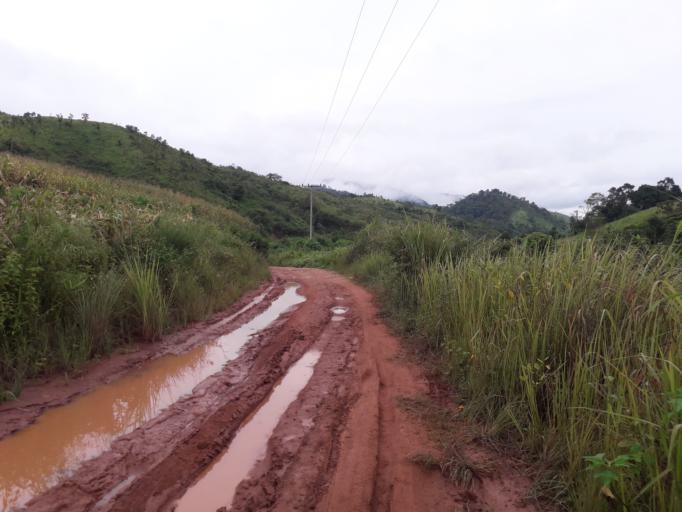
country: CN
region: Yunnan
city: Menglie
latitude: 22.2586
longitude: 101.5939
